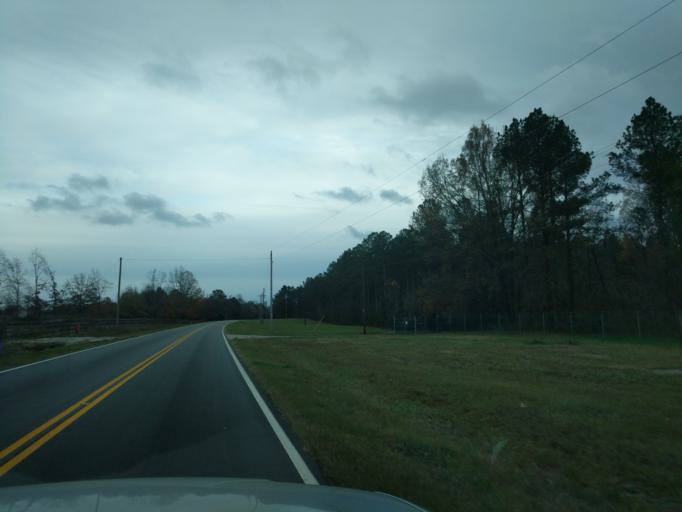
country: US
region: South Carolina
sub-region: Laurens County
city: Laurens
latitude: 34.3949
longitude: -82.0194
